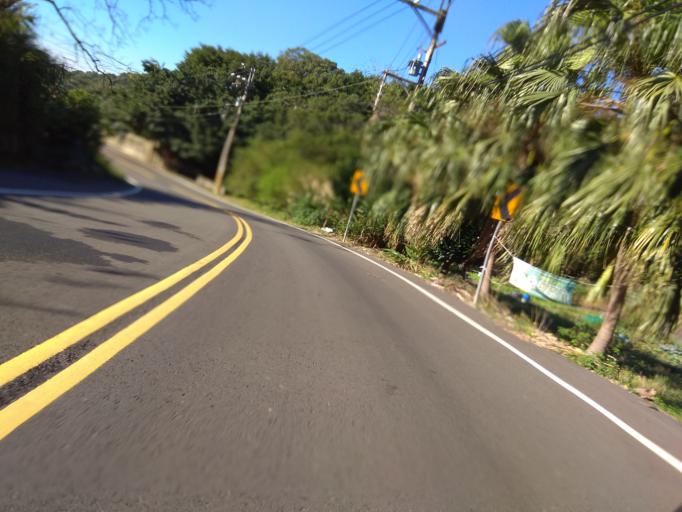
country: TW
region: Taiwan
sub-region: Hsinchu
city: Zhubei
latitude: 24.8563
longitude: 121.1492
